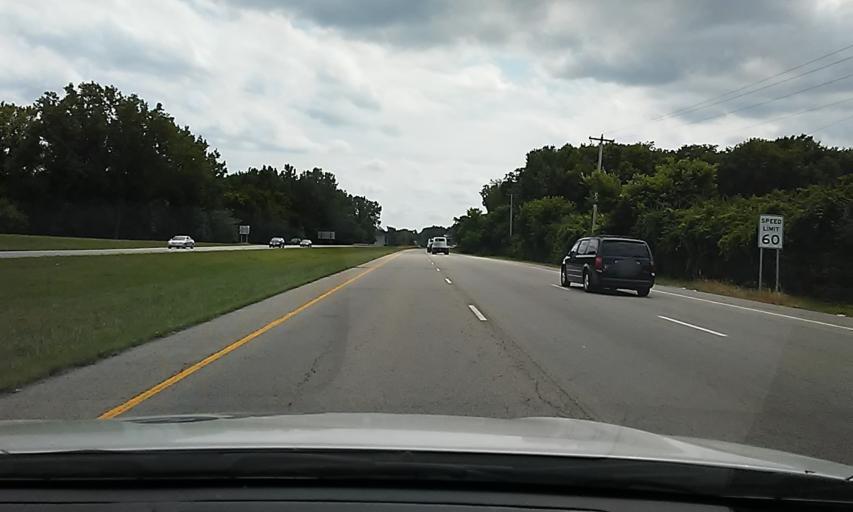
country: US
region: Ohio
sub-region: Greene County
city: Wright-Patterson AFB
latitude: 39.8432
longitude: -84.0592
